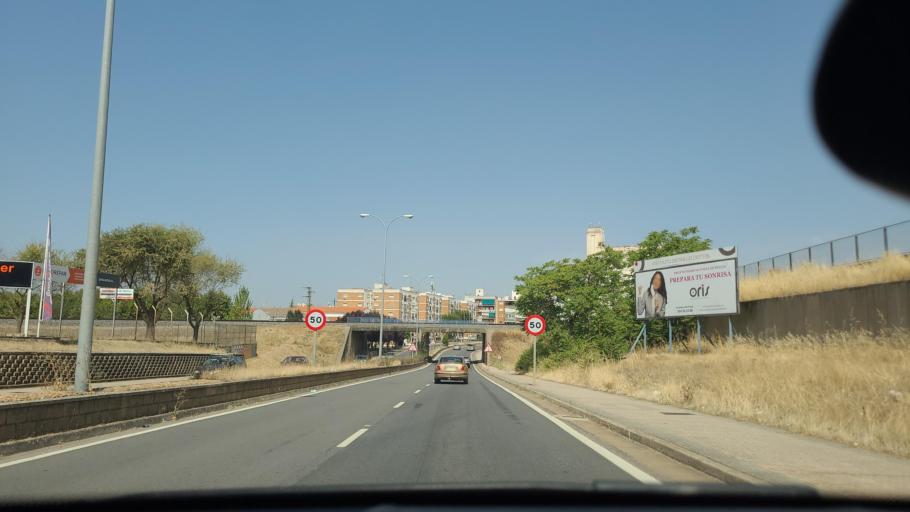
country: ES
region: Extremadura
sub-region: Provincia de Badajoz
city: Zafra
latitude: 38.4219
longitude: -6.4094
